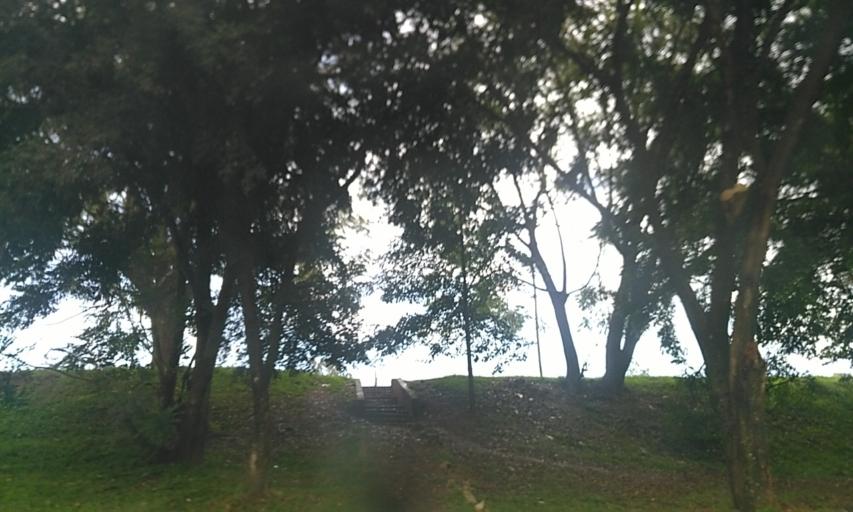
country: UG
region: Central Region
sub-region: Kampala District
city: Kampala
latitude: 0.3249
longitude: 32.5948
